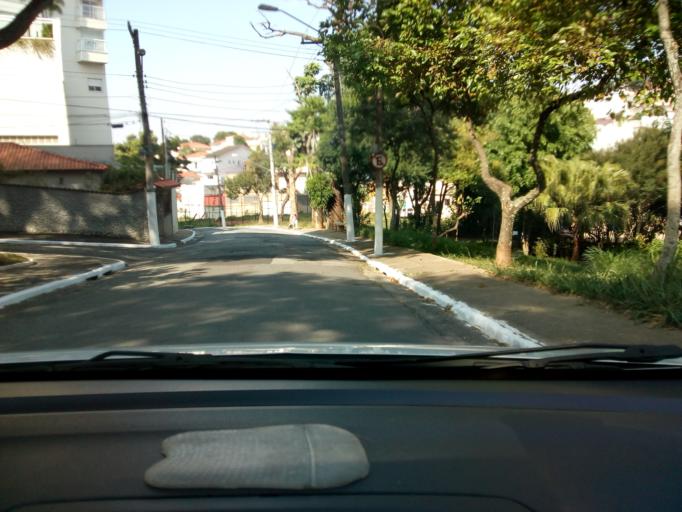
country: BR
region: Sao Paulo
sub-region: Sao Paulo
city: Sao Paulo
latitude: -23.5816
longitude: -46.6195
